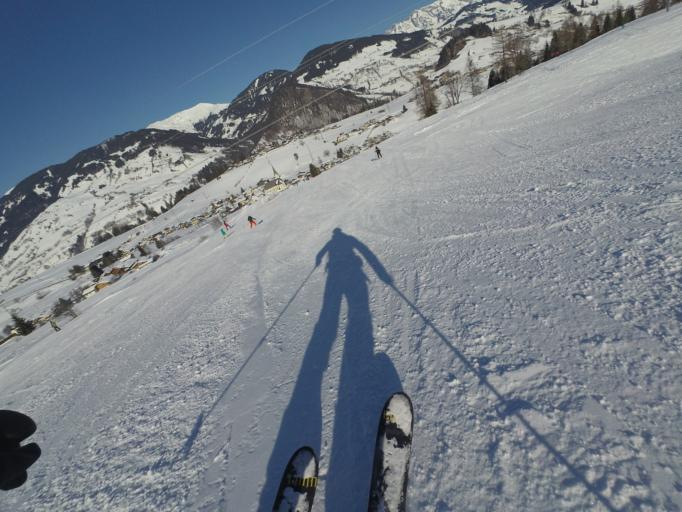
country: AT
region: Salzburg
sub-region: Politischer Bezirk Zell am See
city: Taxenbach
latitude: 47.2854
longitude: 13.0043
